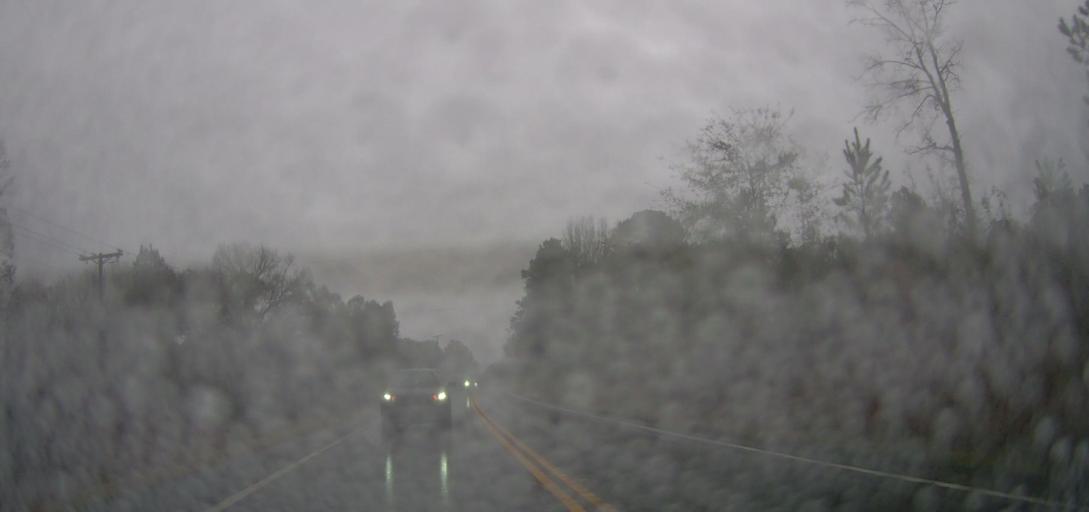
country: US
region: Georgia
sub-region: Putnam County
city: Eatonton
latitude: 33.2270
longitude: -83.4313
